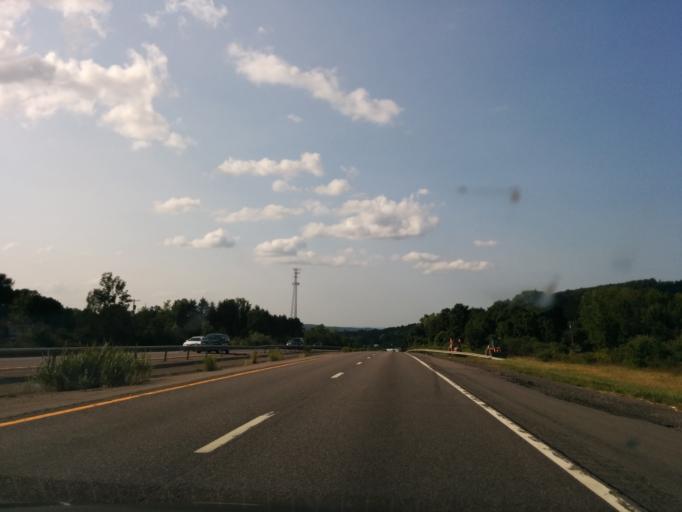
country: US
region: New York
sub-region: Onondaga County
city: Nedrow
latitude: 42.9239
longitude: -76.1229
